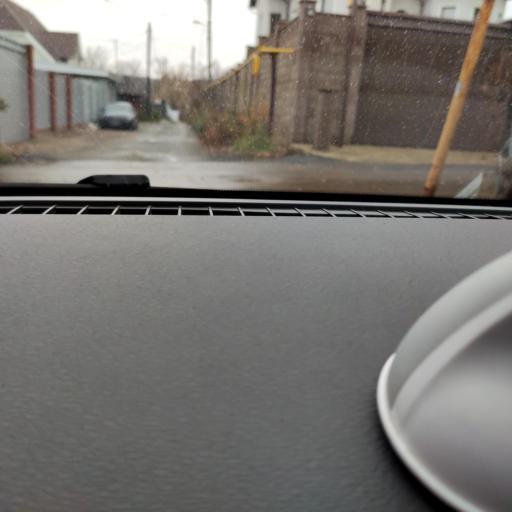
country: RU
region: Samara
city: Samara
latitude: 53.2742
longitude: 50.2109
